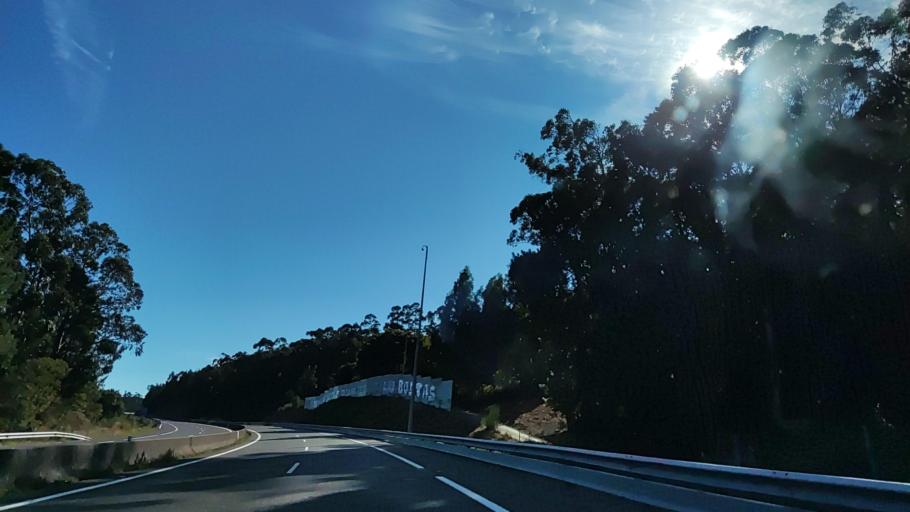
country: ES
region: Galicia
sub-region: Provincia da Coruna
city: Boiro
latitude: 42.6210
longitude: -8.9491
